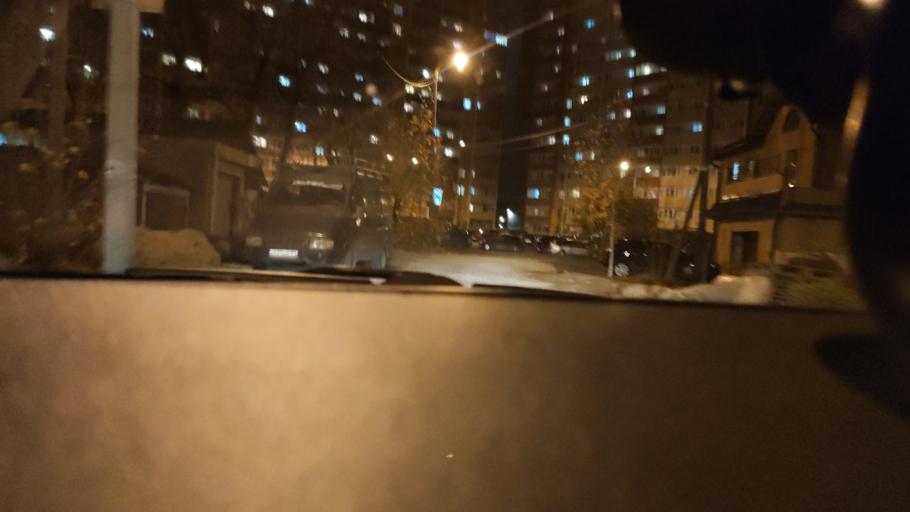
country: RU
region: Perm
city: Perm
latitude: 57.9854
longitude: 56.2953
